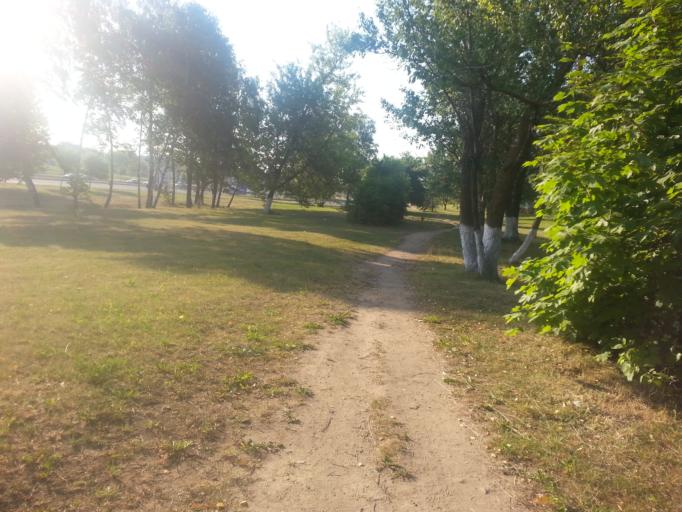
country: BY
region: Minsk
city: Vyaliki Trastsyanets
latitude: 53.8541
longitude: 27.6917
